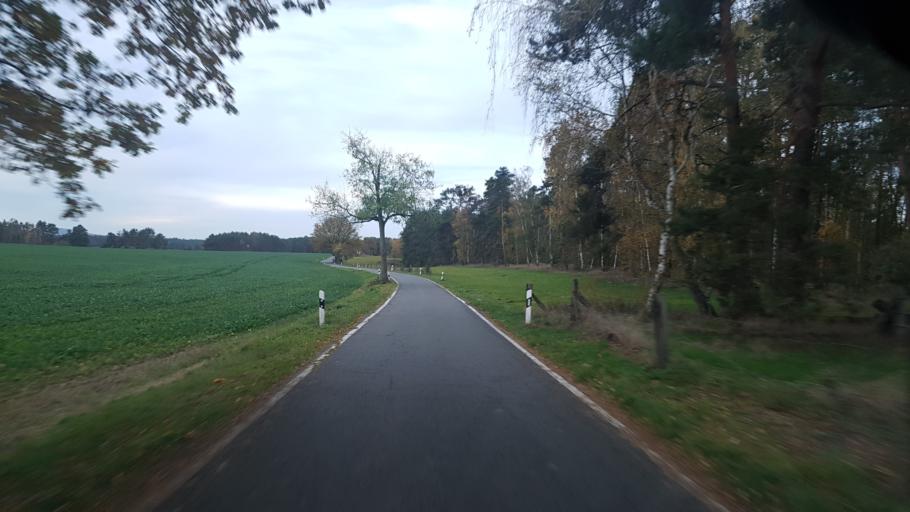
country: DE
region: Saxony
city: Cavertitz
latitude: 51.4044
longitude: 13.0961
